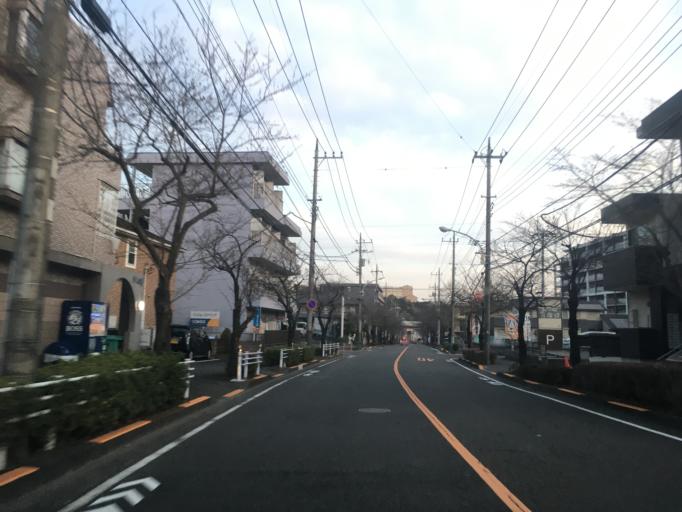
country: JP
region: Tokyo
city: Hino
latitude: 35.6126
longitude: 139.3846
